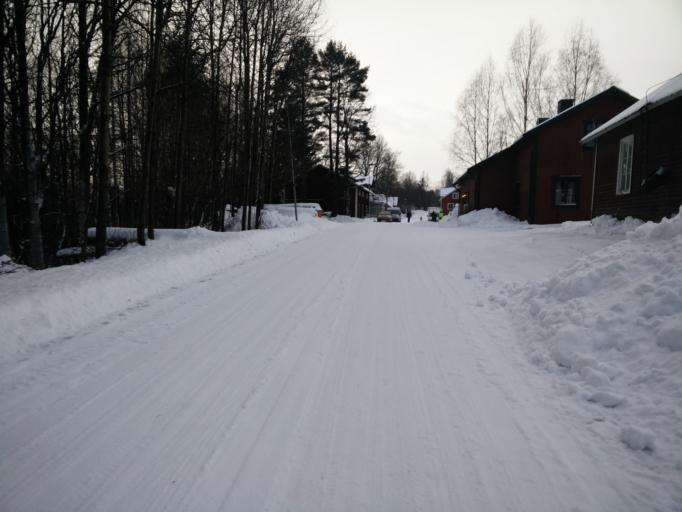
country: SE
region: Vaesternorrland
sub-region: Sundsvalls Kommun
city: Kvissleby
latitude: 62.2929
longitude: 17.3779
